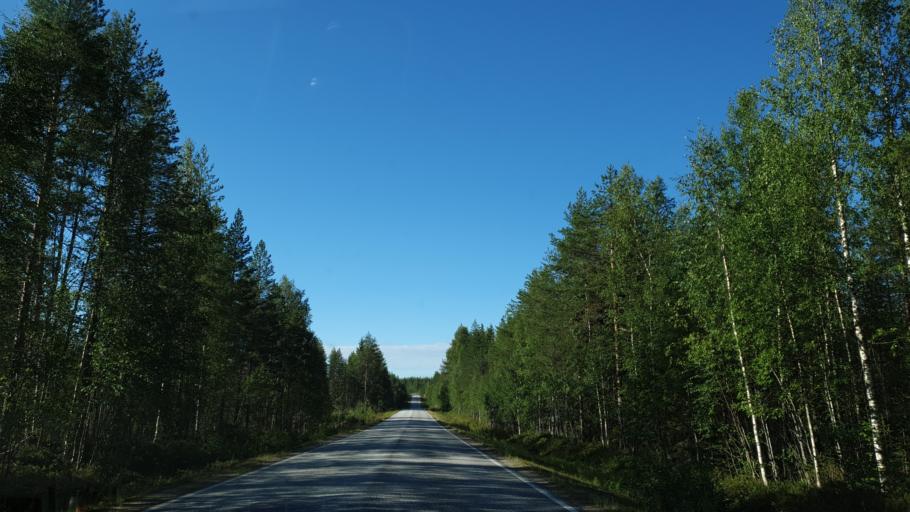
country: FI
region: Kainuu
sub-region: Kehys-Kainuu
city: Kuhmo
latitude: 64.3445
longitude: 29.4869
